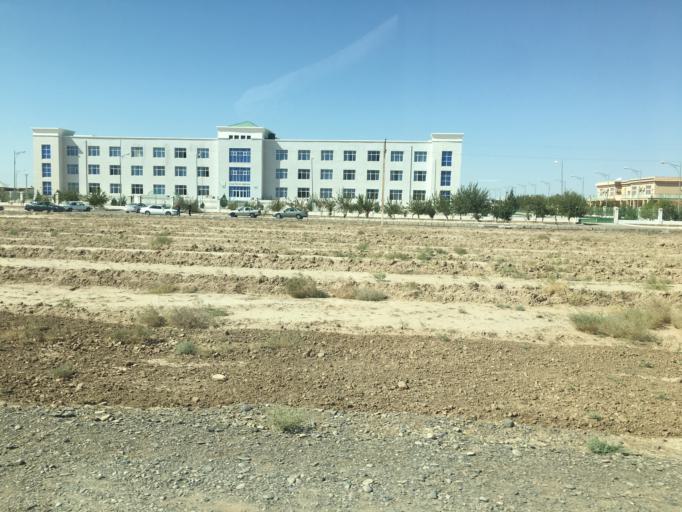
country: IR
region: Razavi Khorasan
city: Sarakhs
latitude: 36.5495
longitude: 61.2156
